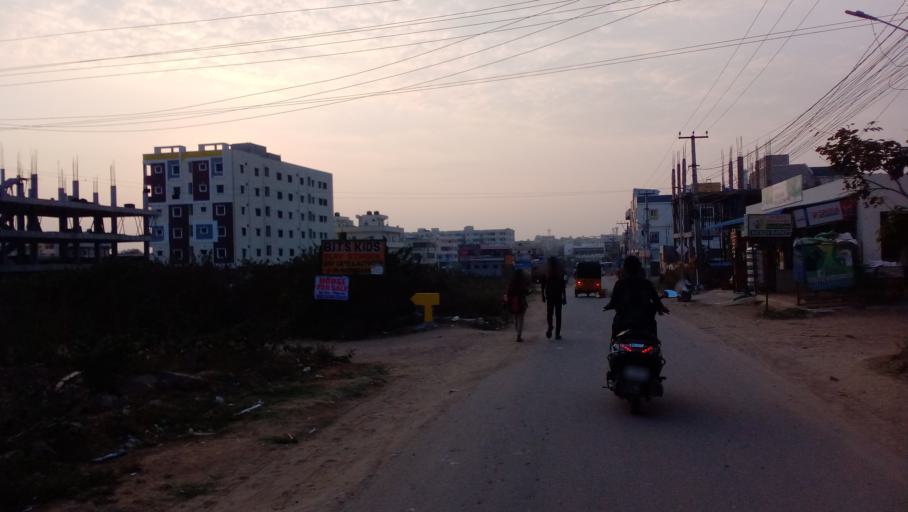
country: IN
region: Telangana
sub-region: Medak
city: Serilingampalle
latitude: 17.5178
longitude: 78.3179
